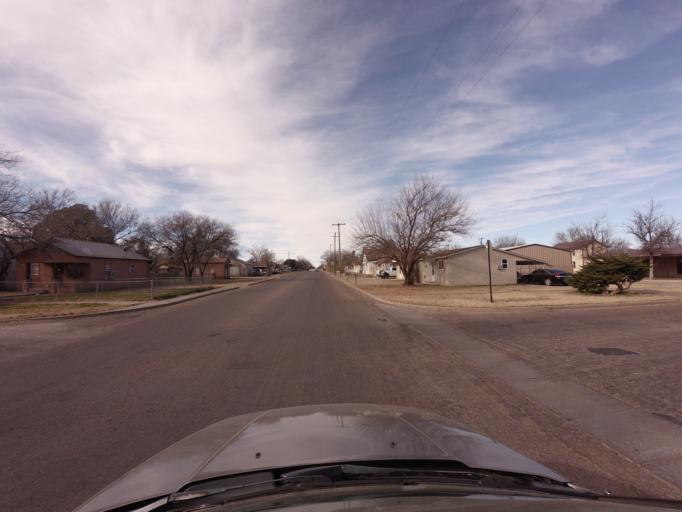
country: US
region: New Mexico
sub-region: Curry County
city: Clovis
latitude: 34.4079
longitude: -103.2002
